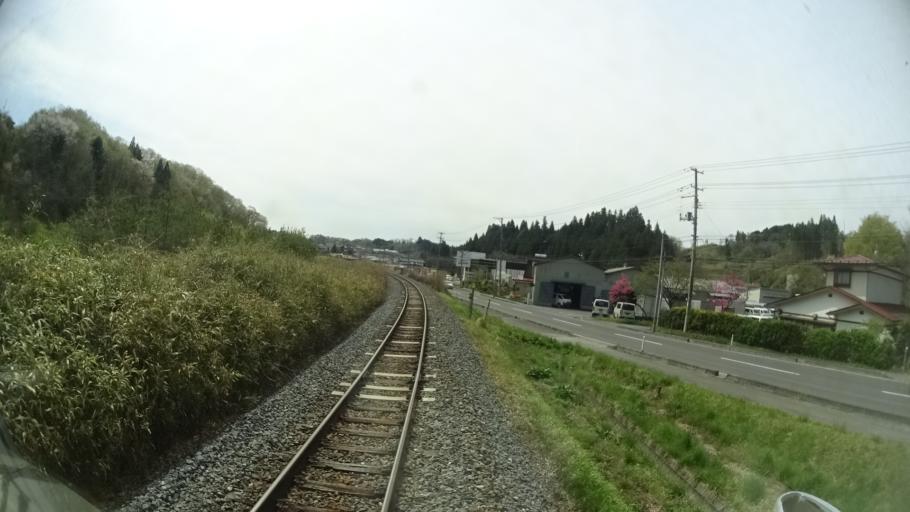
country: JP
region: Iwate
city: Ichinoseki
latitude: 38.9268
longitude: 141.3399
